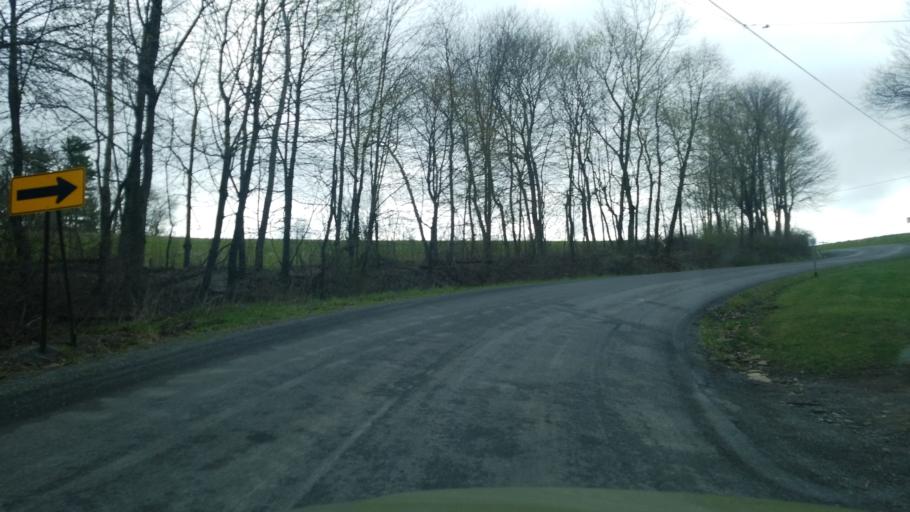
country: US
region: Pennsylvania
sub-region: Clearfield County
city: Clearfield
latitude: 41.0836
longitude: -78.4042
